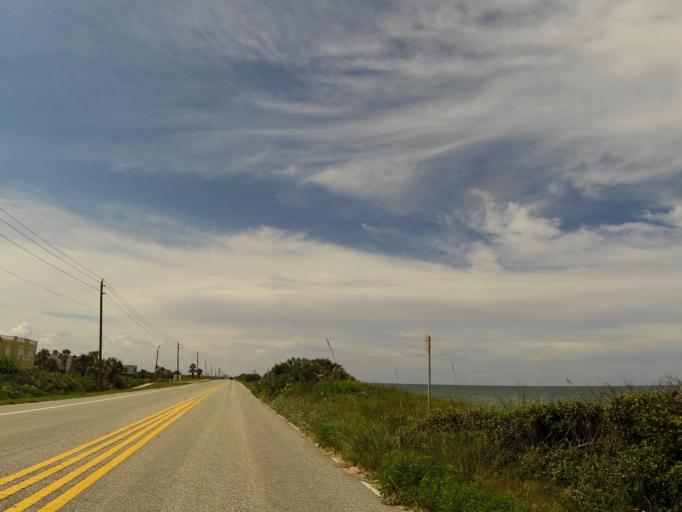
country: US
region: Florida
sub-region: Volusia County
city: Ormond-by-the-Sea
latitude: 29.3878
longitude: -81.0847
